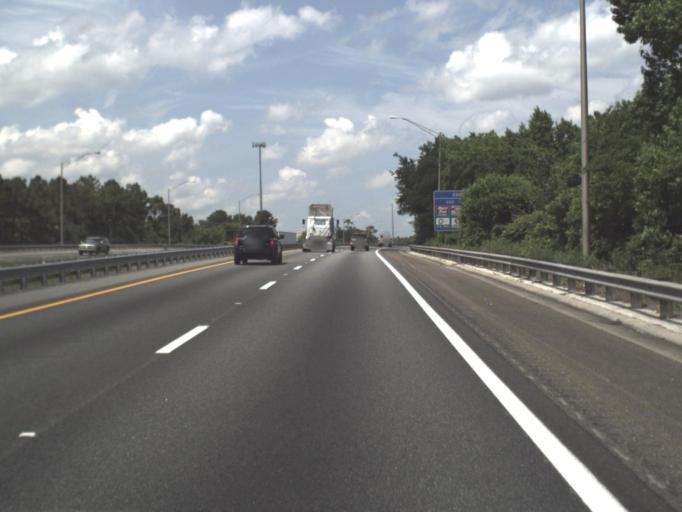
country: US
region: Florida
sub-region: Nassau County
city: Nassau Village-Ratliff
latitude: 30.4059
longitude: -81.7533
